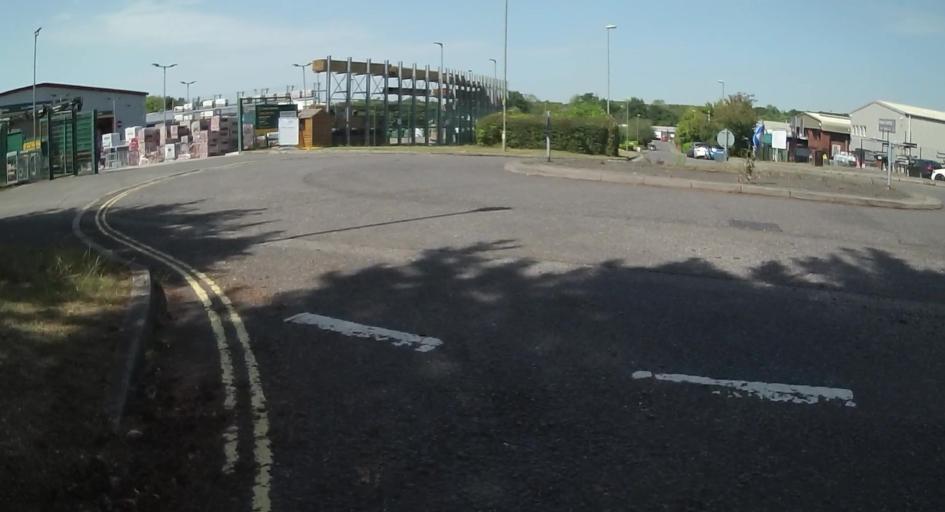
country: GB
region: England
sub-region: Hampshire
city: Basingstoke
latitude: 51.2756
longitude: -1.0643
